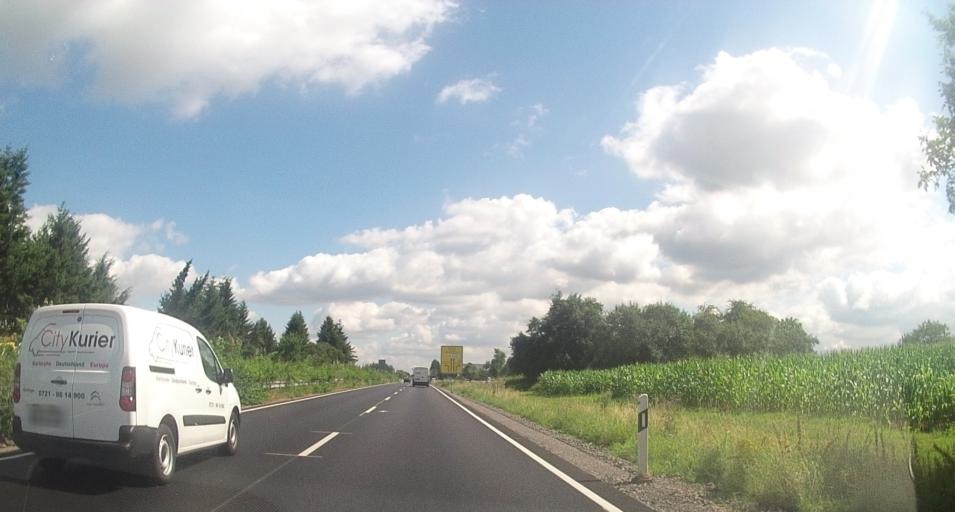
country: DE
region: Baden-Wuerttemberg
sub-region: Karlsruhe Region
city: Rheinstetten
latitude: 48.9557
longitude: 8.2948
